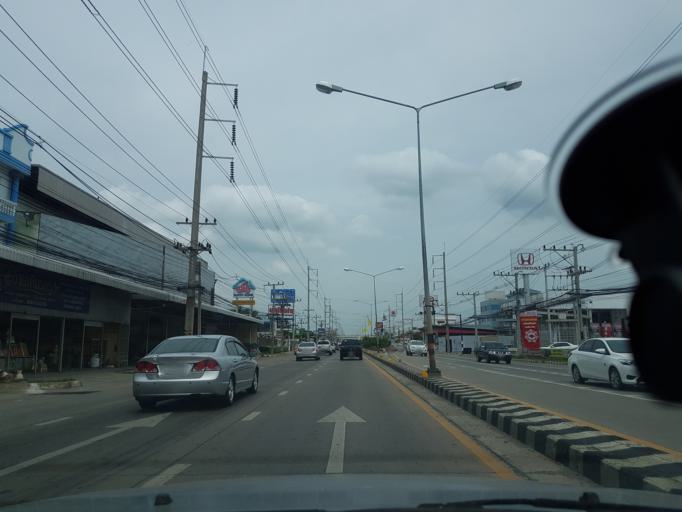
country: TH
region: Lop Buri
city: Lop Buri
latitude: 14.7856
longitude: 100.6811
